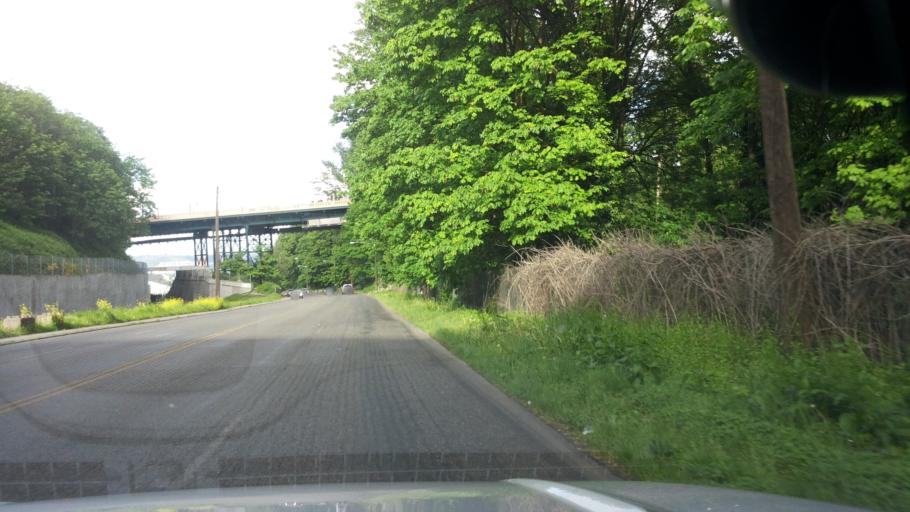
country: US
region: Washington
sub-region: Pierce County
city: Tacoma
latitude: 47.2335
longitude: -122.4430
